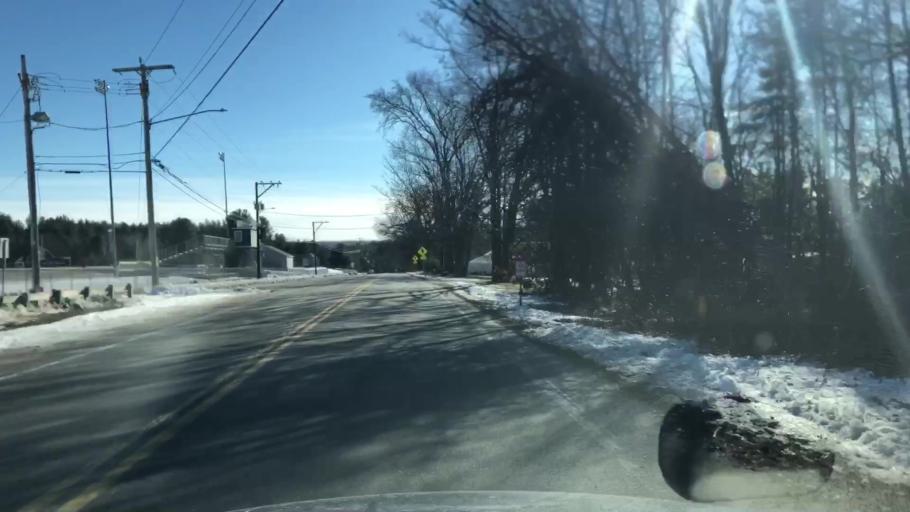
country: US
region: New Hampshire
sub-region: Hillsborough County
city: Milford
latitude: 42.8283
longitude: -71.6606
